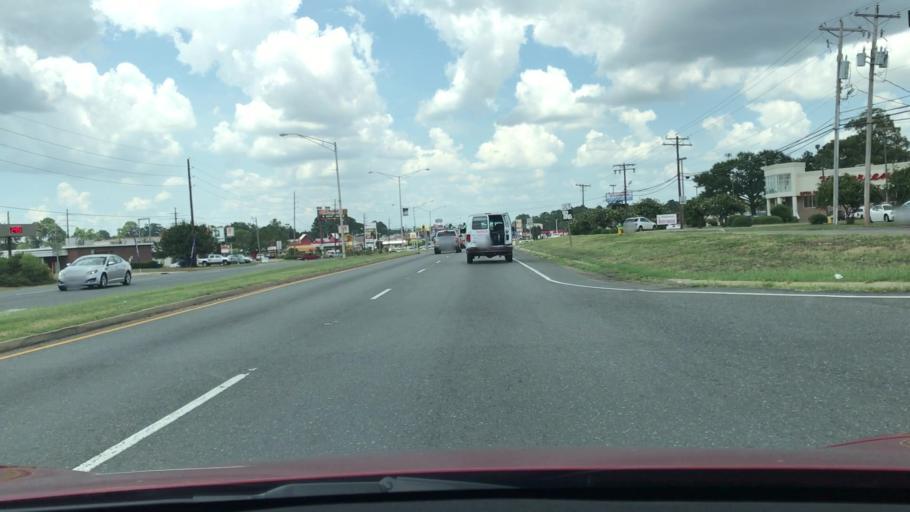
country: US
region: Louisiana
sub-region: De Soto Parish
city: Stonewall
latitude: 32.4004
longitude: -93.8058
